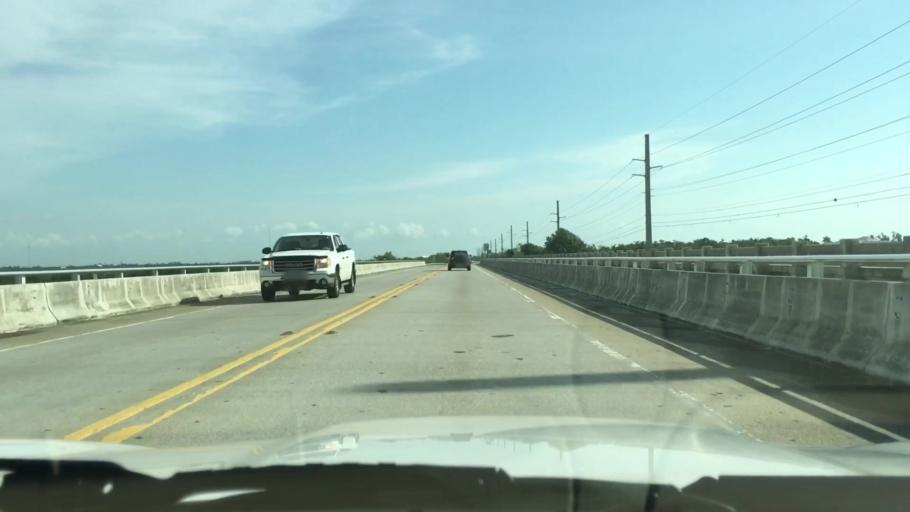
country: US
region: Florida
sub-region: Monroe County
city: Cudjoe Key
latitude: 24.6619
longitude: -81.5162
